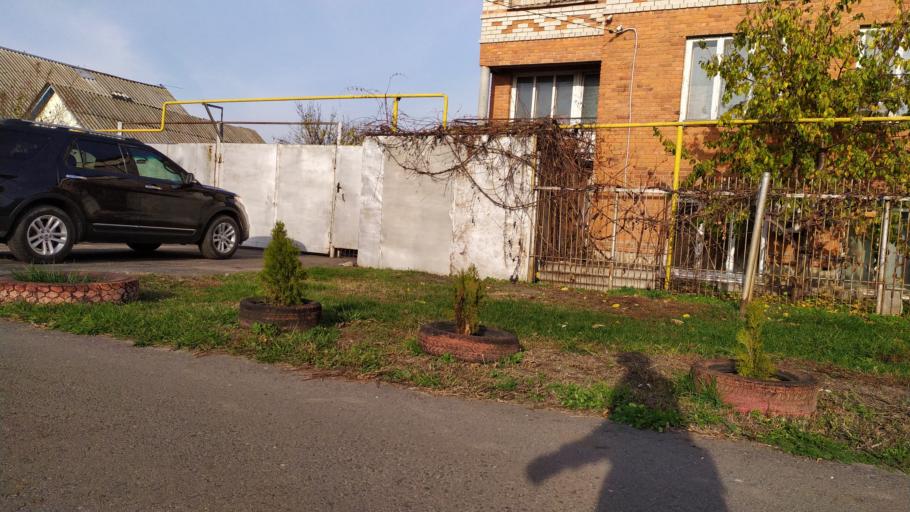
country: RU
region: Kursk
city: Kursk
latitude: 51.6428
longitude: 36.1488
